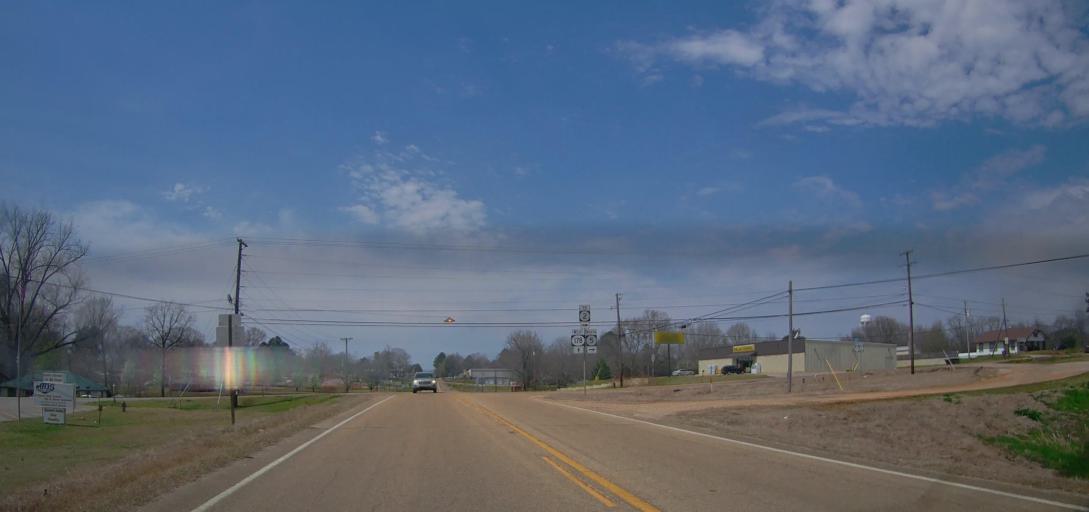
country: US
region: Mississippi
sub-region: Union County
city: New Albany
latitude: 34.6177
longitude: -89.1836
